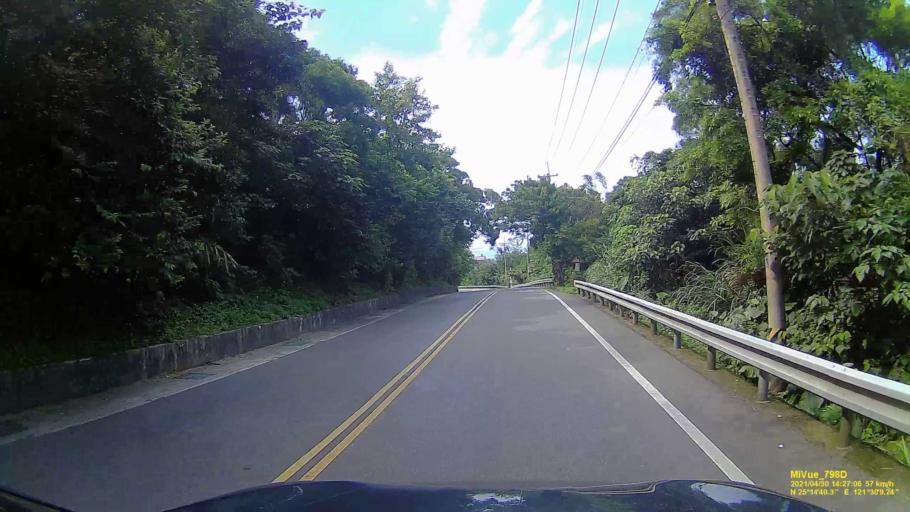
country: TW
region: Taipei
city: Taipei
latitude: 25.2449
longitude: 121.5025
